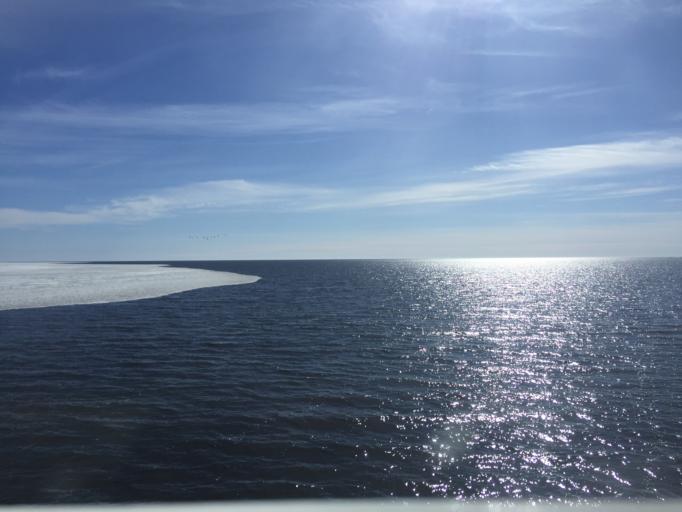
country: EE
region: Laeaene
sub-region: Haapsalu linn
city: Haapsalu
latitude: 58.5761
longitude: 23.4781
